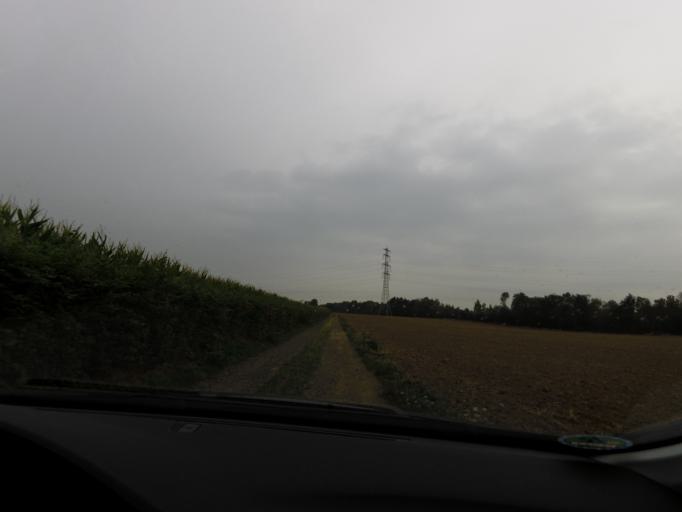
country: NL
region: Limburg
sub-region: Gemeente Simpelveld
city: Simpelveld
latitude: 50.8498
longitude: 5.9758
